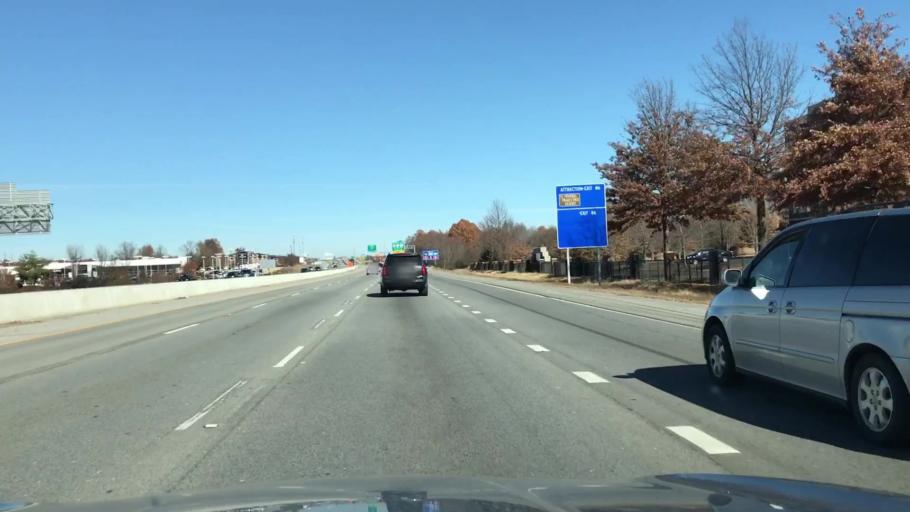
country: US
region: Arkansas
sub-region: Benton County
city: Bentonville
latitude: 36.3437
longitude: -94.1809
